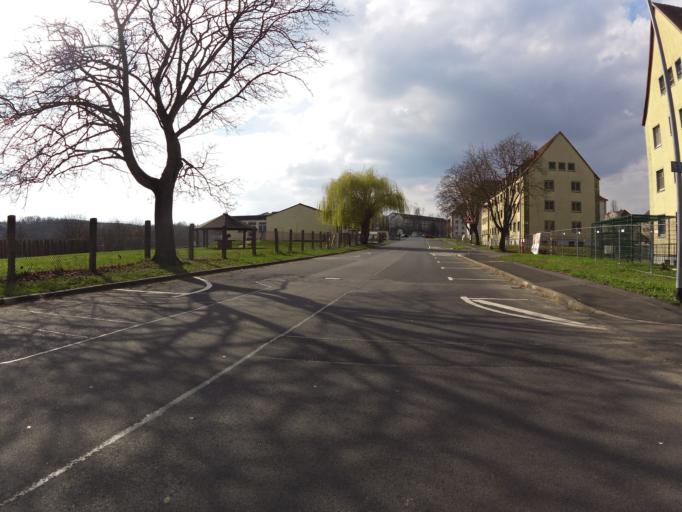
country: DE
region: Bavaria
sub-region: Regierungsbezirk Unterfranken
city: Kitzingen
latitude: 49.7395
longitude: 10.1426
